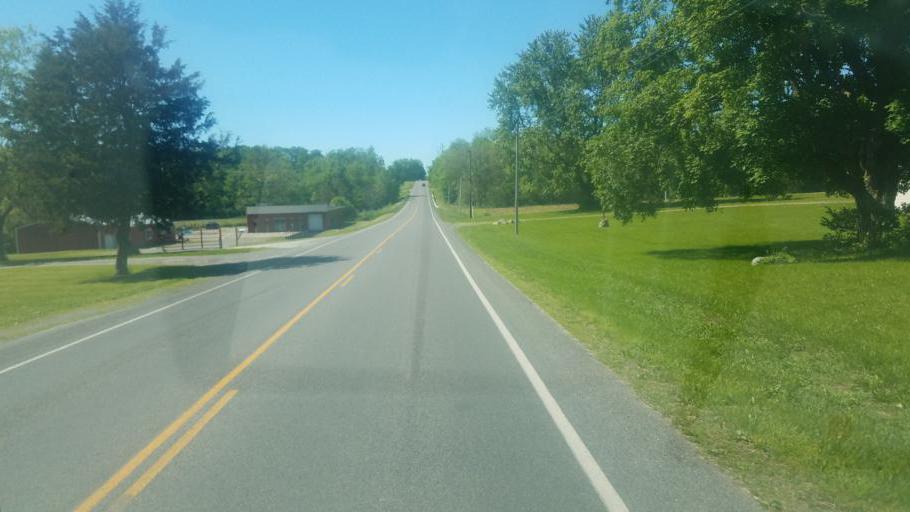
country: US
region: Ohio
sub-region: Logan County
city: Bellefontaine
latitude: 40.3721
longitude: -83.7775
